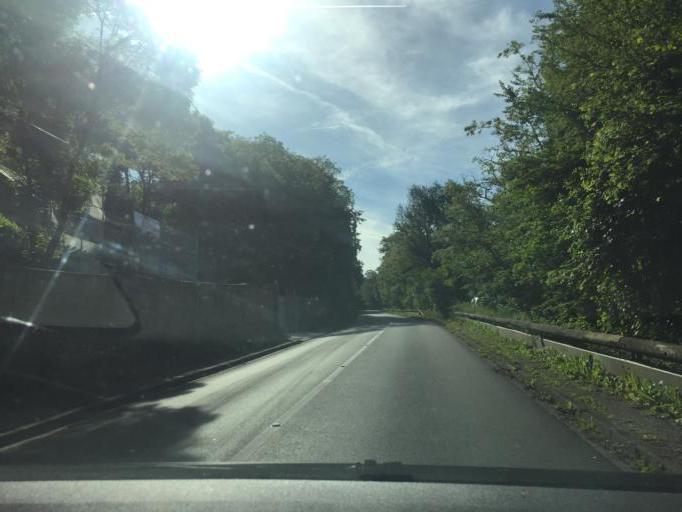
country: FR
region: Ile-de-France
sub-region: Departement des Yvelines
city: Chateaufort
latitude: 48.7326
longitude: 2.0970
